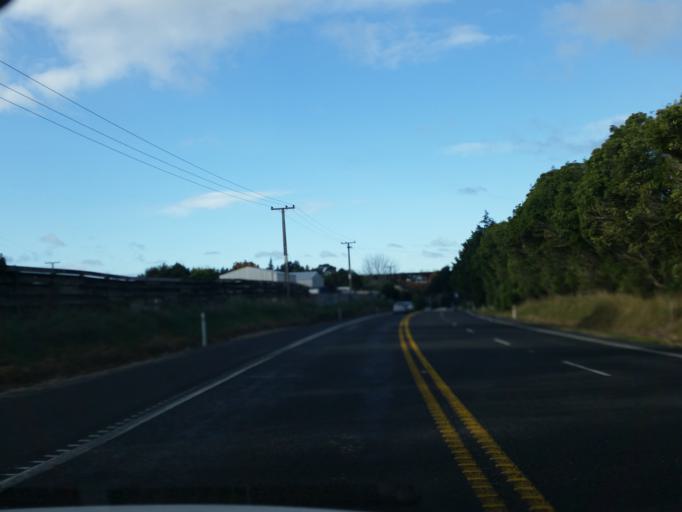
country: NZ
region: Bay of Plenty
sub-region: Tauranga City
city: Tauranga
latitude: -37.6972
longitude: 176.0601
